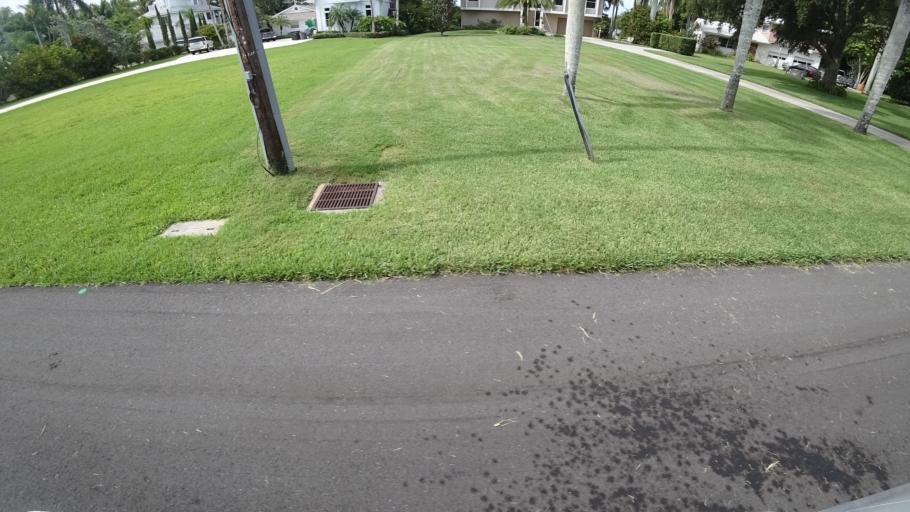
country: US
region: Florida
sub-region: Manatee County
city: Cortez
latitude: 27.4589
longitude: -82.6661
